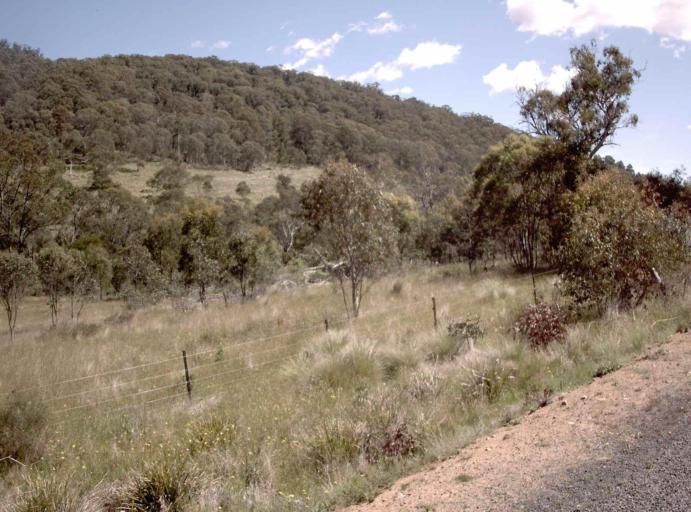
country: AU
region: New South Wales
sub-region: Bombala
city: Bombala
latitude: -37.0444
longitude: 148.8141
